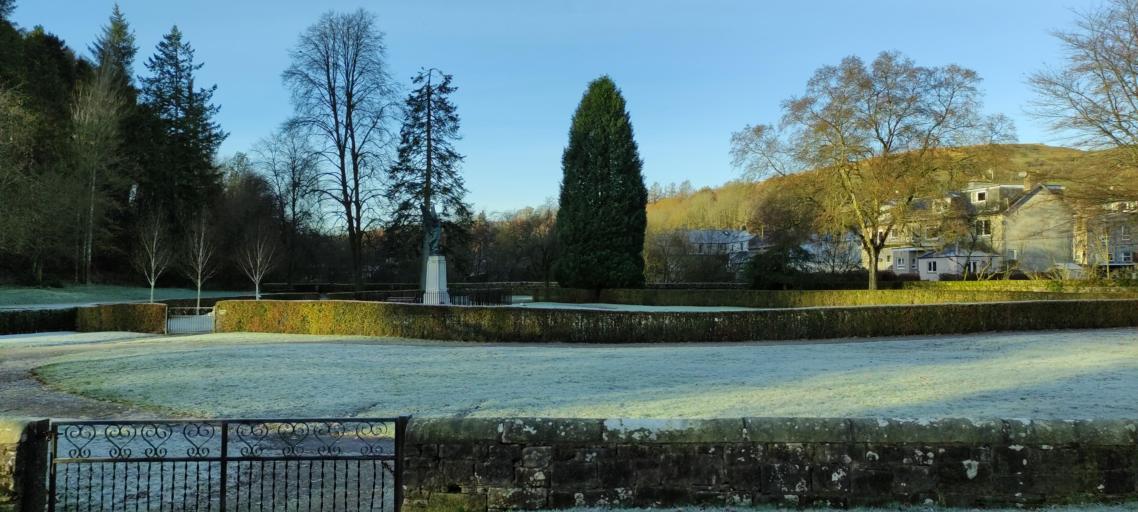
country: GB
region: Scotland
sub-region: Dumfries and Galloway
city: Langholm
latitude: 55.1502
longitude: -3.0036
